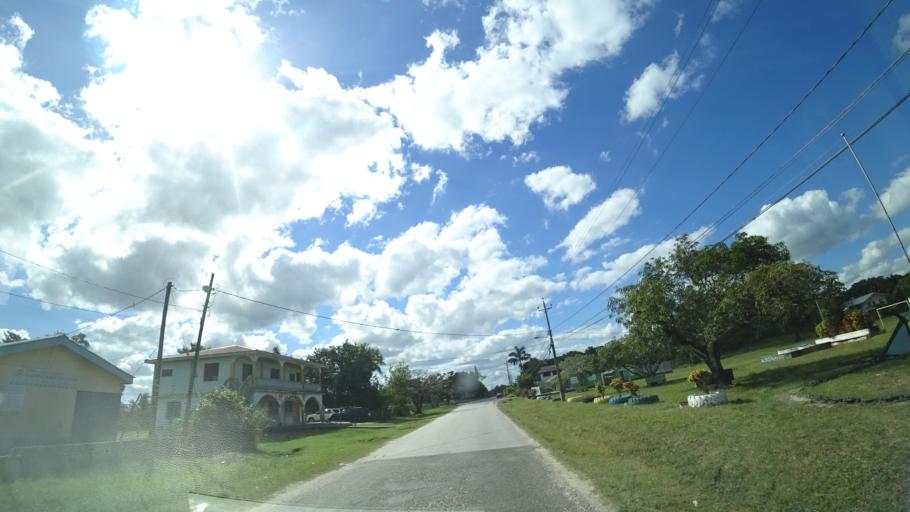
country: BZ
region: Belize
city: Belize City
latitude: 17.5688
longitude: -88.4076
